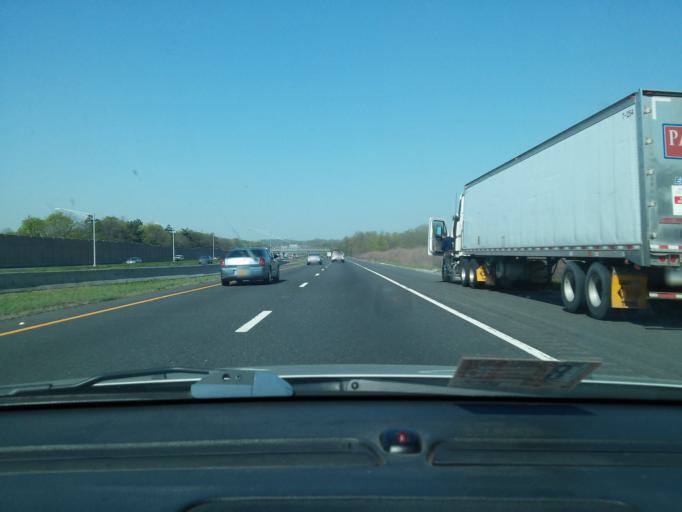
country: US
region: New Jersey
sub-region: Essex County
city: Maplewood
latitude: 40.7145
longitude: -74.2901
